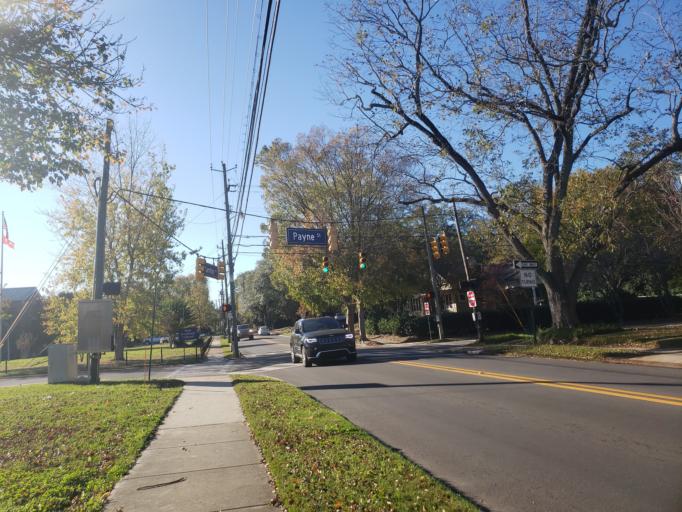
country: US
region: Alabama
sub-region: Lee County
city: Auburn
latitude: 32.5988
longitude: -85.4760
